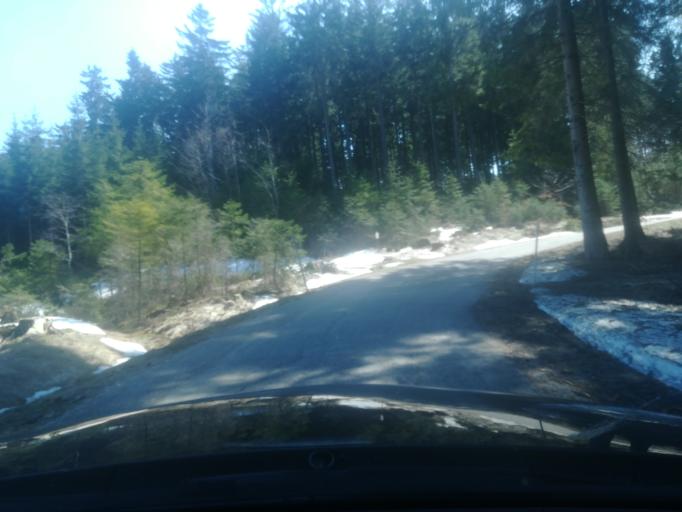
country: AT
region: Lower Austria
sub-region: Politischer Bezirk Zwettl
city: Langschlag
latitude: 48.5090
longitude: 14.8517
